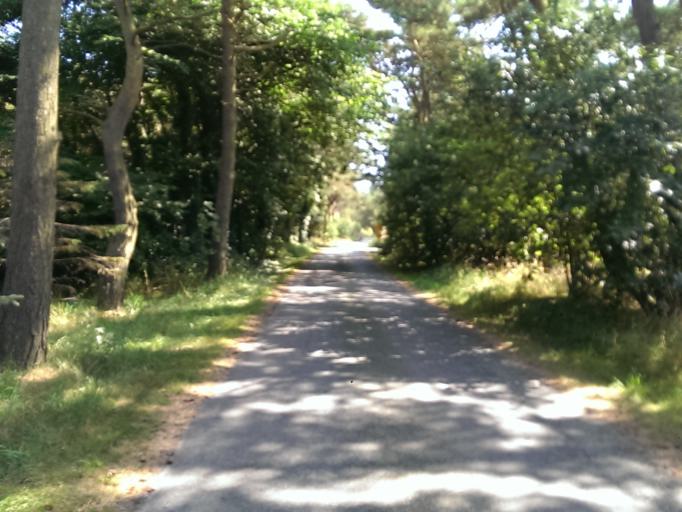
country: SE
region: Skane
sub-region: Simrishamns Kommun
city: Simrishamn
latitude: 55.4299
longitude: 14.2232
